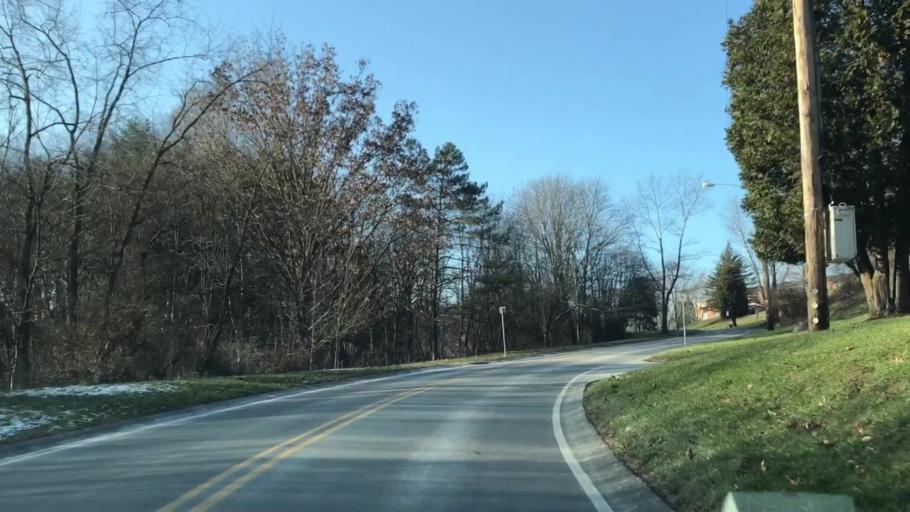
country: US
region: Pennsylvania
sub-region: Allegheny County
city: Allison Park
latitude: 40.5824
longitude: -79.9972
